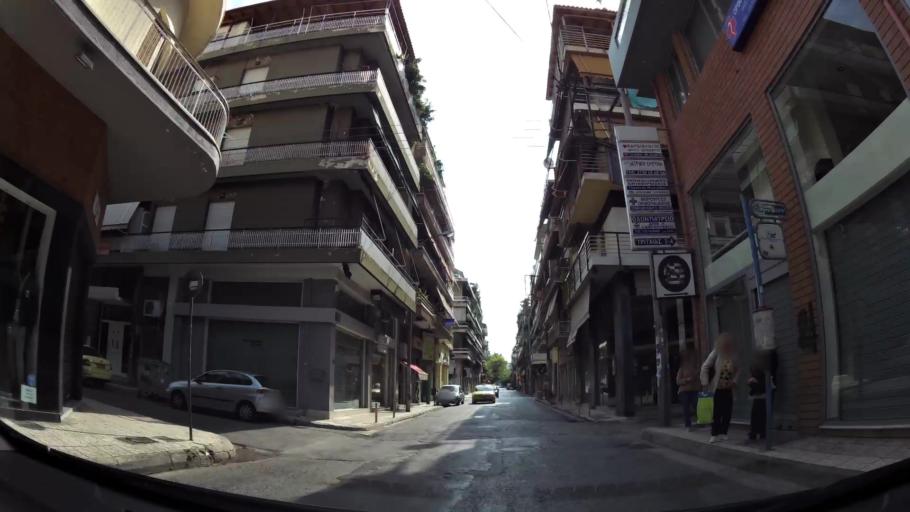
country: GR
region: Attica
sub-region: Nomarchia Athinas
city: Athens
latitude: 37.9899
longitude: 23.7115
